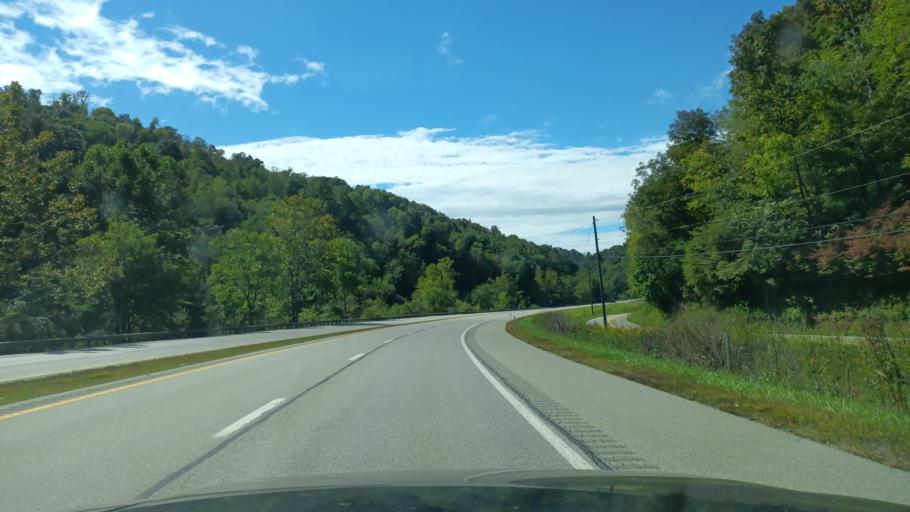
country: US
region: West Virginia
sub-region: Harrison County
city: Salem
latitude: 39.2898
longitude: -80.6376
